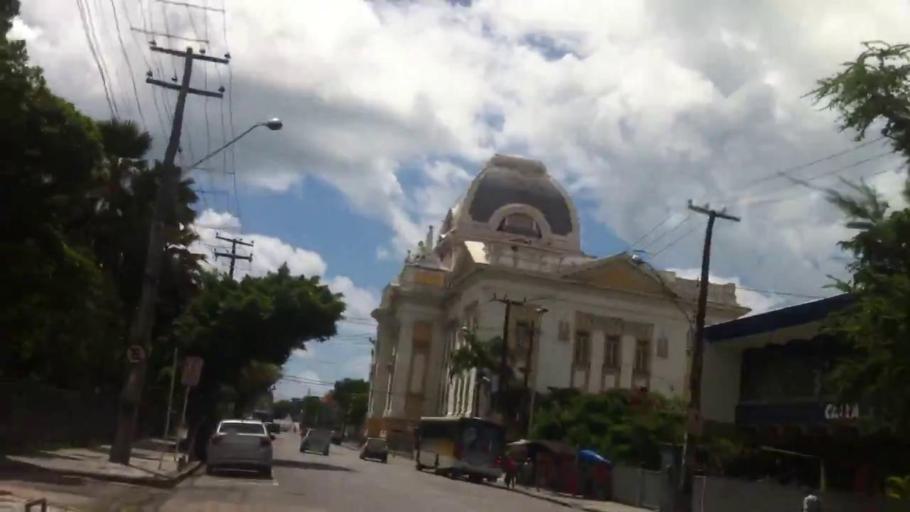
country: BR
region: Pernambuco
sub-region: Recife
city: Recife
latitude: -8.0613
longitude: -34.8778
